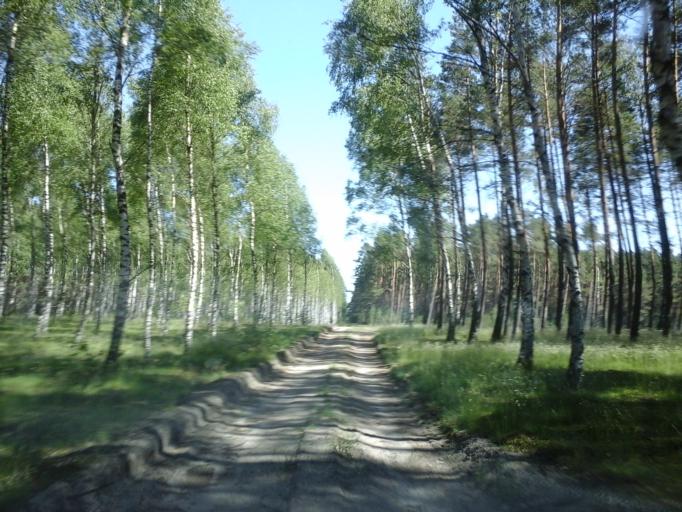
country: PL
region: West Pomeranian Voivodeship
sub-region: Powiat drawski
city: Kalisz Pomorski
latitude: 53.1556
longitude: 15.9503
